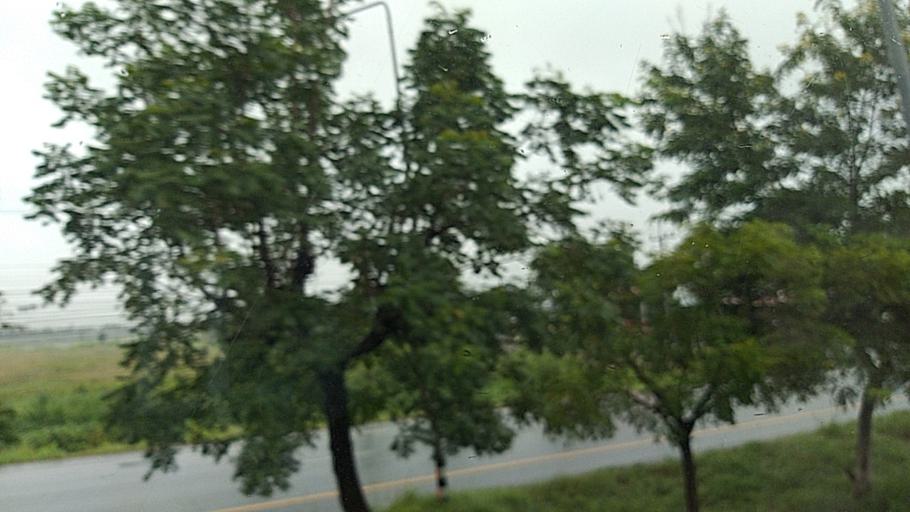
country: TH
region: Nakhon Ratchasima
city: Phimai
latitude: 15.2531
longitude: 102.4064
